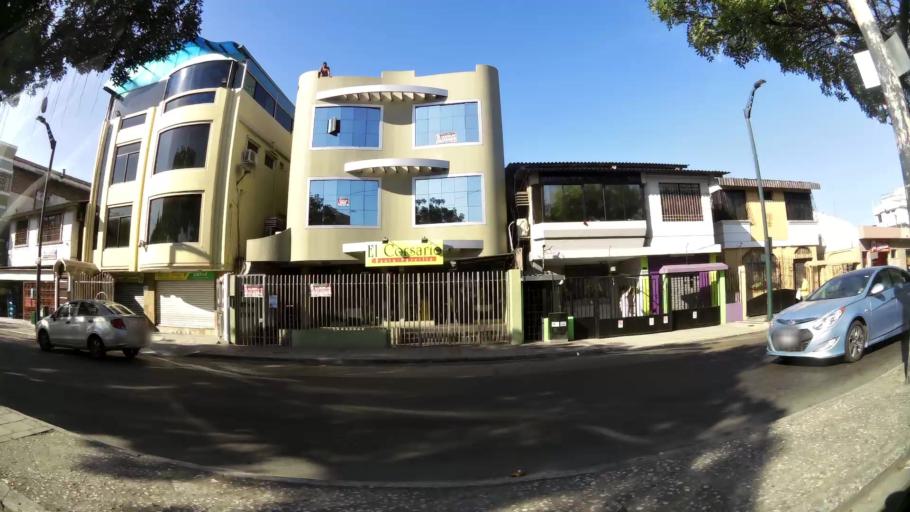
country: EC
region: Guayas
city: Guayaquil
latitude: -2.1717
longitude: -79.8952
